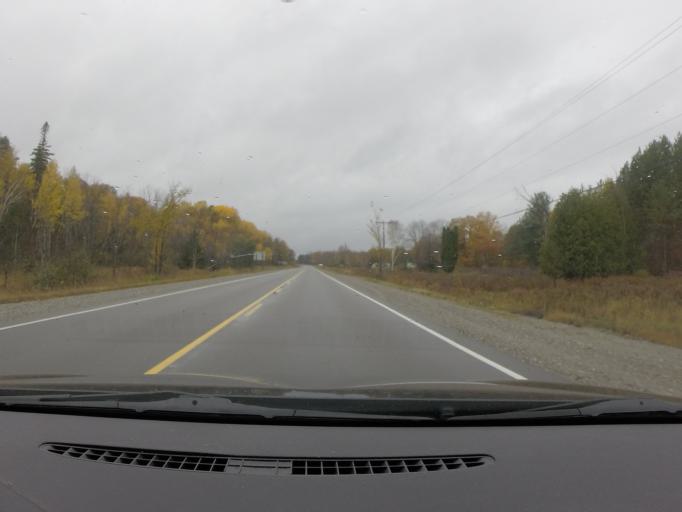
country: CA
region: Ontario
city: Skatepark
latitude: 44.7378
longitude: -76.9395
